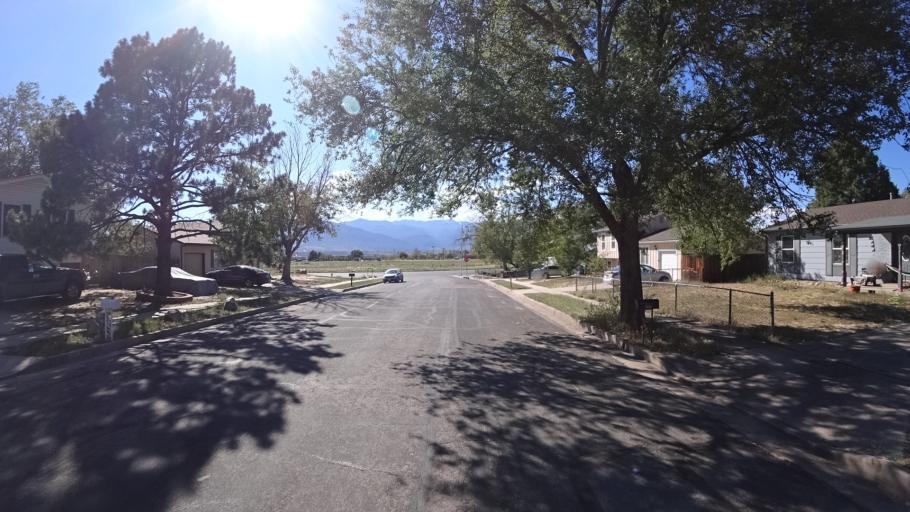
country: US
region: Colorado
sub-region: El Paso County
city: Stratmoor
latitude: 38.7942
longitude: -104.7543
